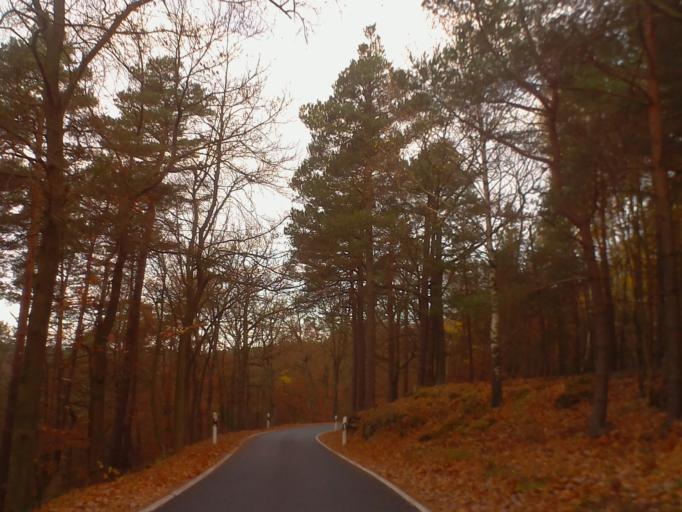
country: DE
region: Rheinland-Pfalz
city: Altleiningen
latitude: 49.4819
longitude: 8.1066
